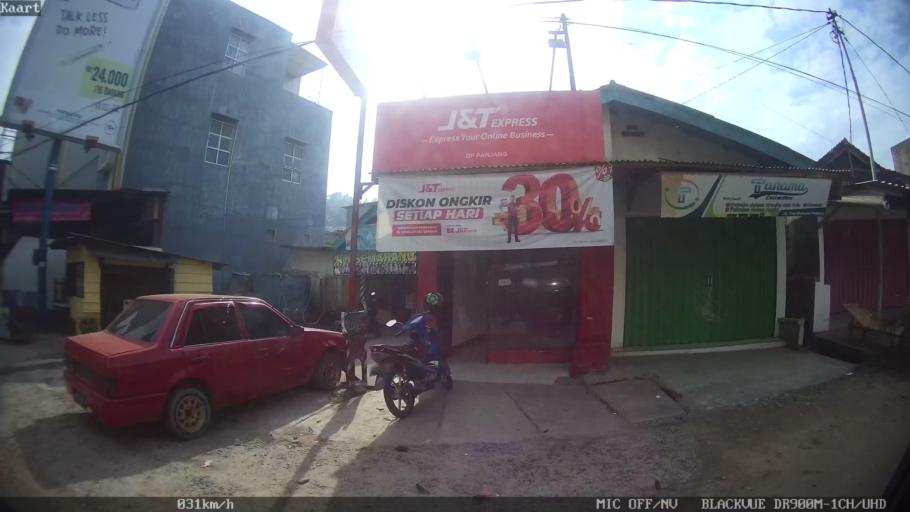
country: ID
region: Lampung
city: Panjang
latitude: -5.4699
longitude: 105.3225
